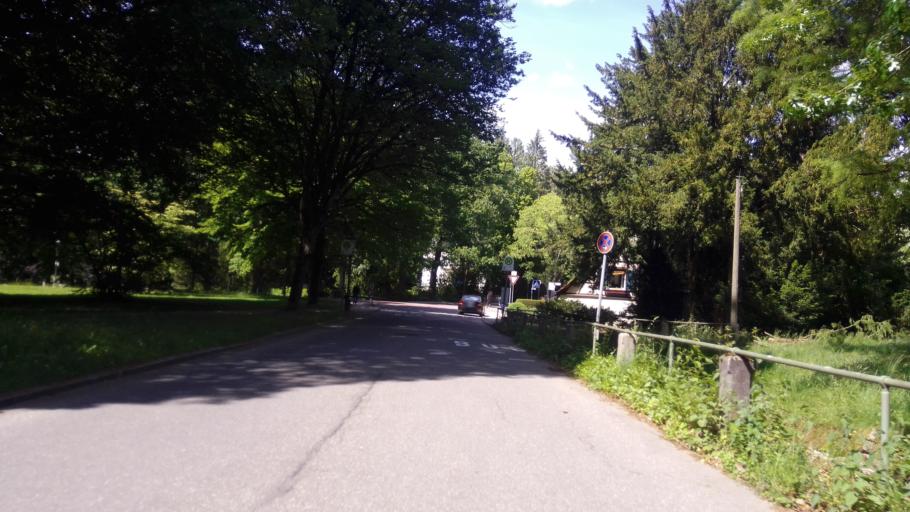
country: DE
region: Baden-Wuerttemberg
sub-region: Karlsruhe Region
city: Baden-Baden
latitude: 48.7501
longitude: 8.2449
